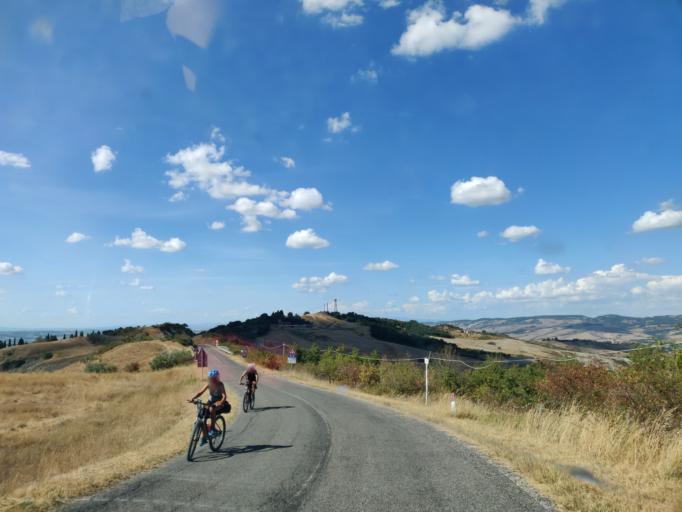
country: IT
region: Tuscany
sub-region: Provincia di Siena
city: Radicofani
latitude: 42.9505
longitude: 11.7306
